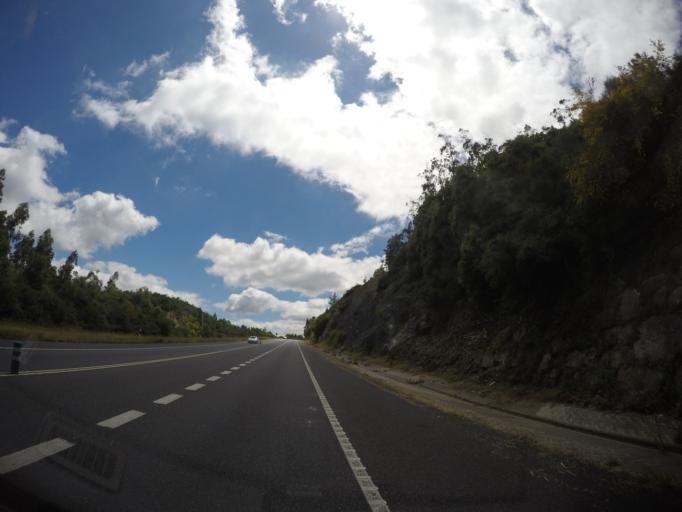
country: ES
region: Aragon
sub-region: Provincia de Zaragoza
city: El Burgo de Ebro
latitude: 41.5450
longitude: -0.7404
